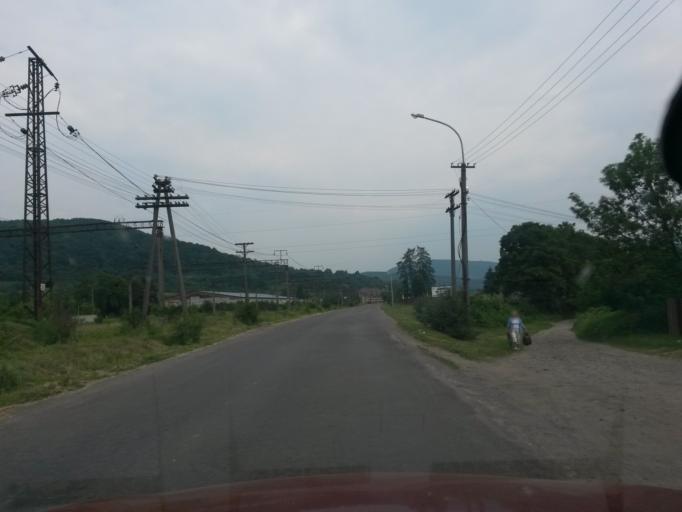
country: UA
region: Zakarpattia
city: Velykyi Bereznyi
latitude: 48.9026
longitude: 22.4587
